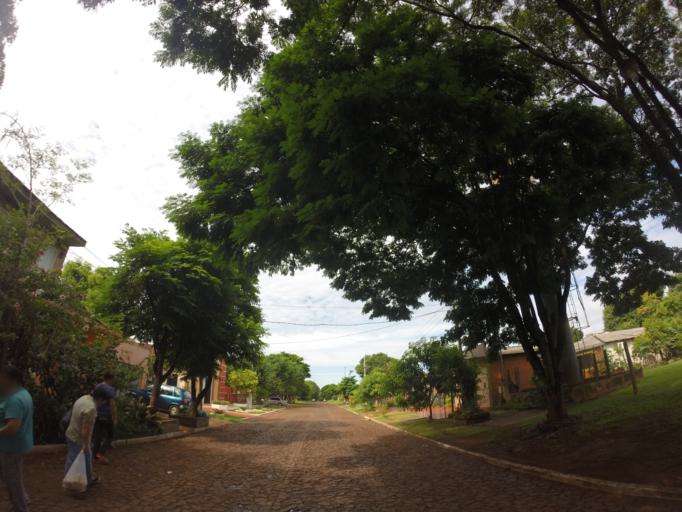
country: PY
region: Alto Parana
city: Ciudad del Este
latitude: -25.4074
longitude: -54.6435
